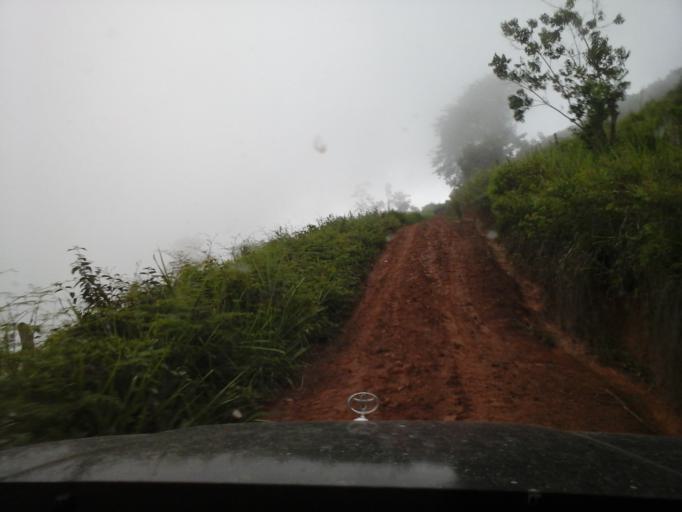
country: CO
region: Cesar
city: Agustin Codazzi
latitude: 9.9589
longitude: -73.0614
